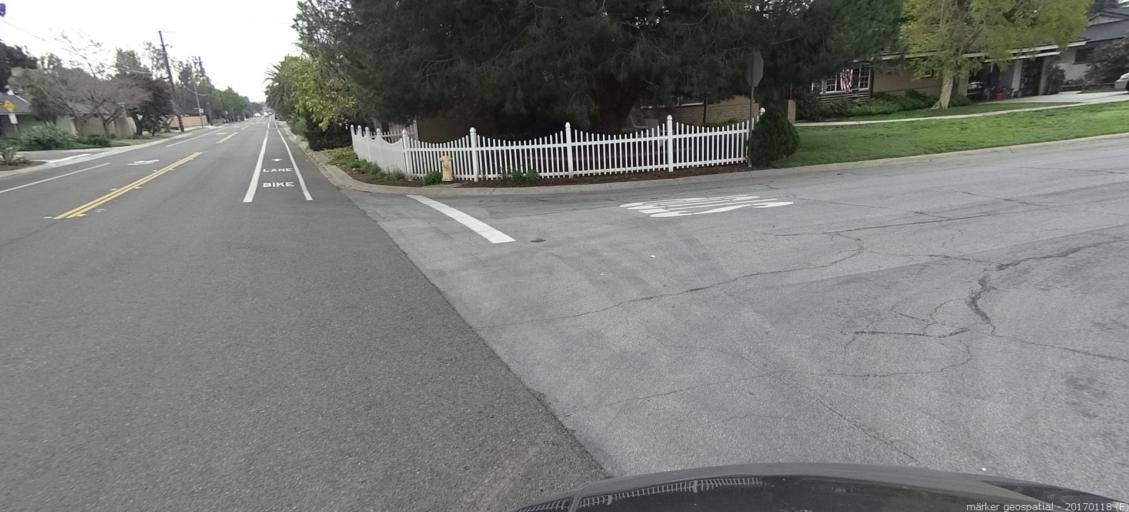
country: US
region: California
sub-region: Orange County
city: North Tustin
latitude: 33.7497
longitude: -117.7980
